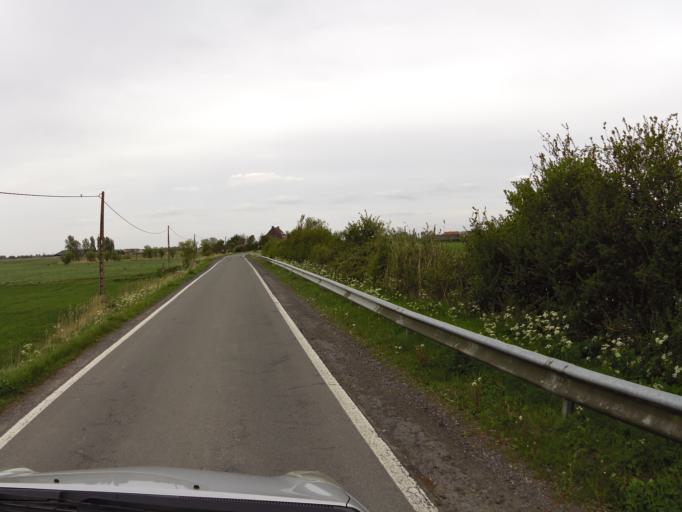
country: BE
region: Flanders
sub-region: Provincie West-Vlaanderen
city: Diksmuide
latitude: 51.0783
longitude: 2.8375
